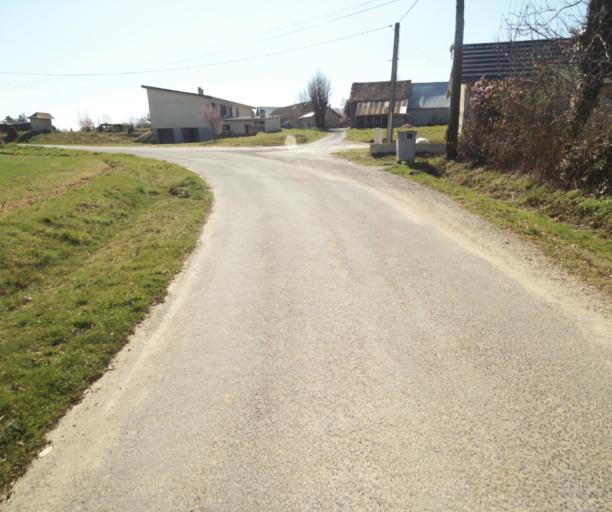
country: FR
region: Limousin
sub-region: Departement de la Correze
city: Saint-Mexant
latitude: 45.3084
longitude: 1.6015
